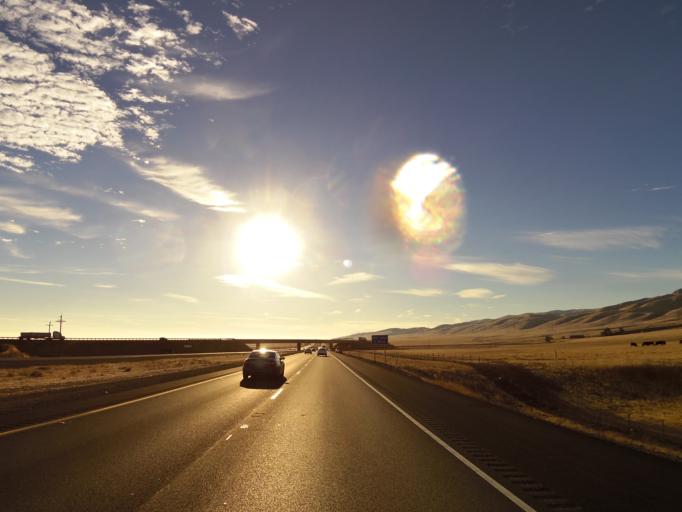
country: US
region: California
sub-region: San Joaquin County
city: Tracy
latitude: 37.6000
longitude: -121.3458
